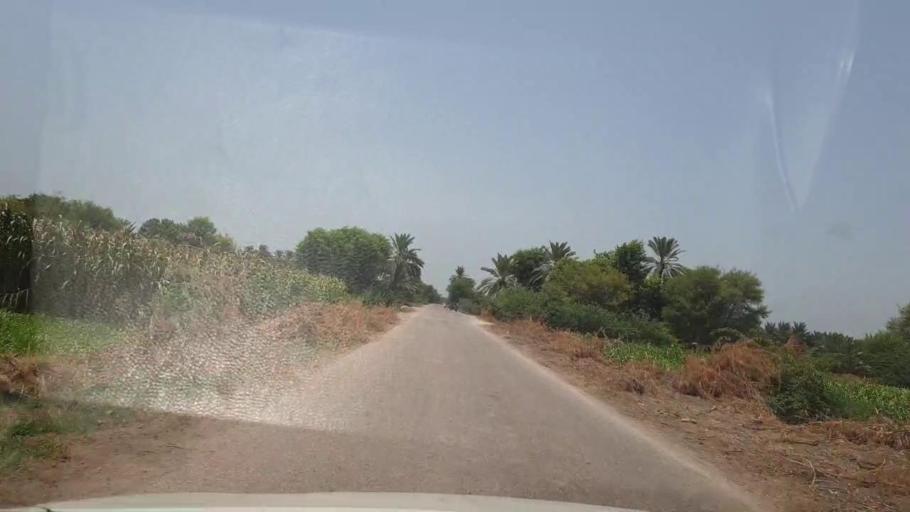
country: PK
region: Sindh
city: Bozdar
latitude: 27.1878
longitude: 68.6126
